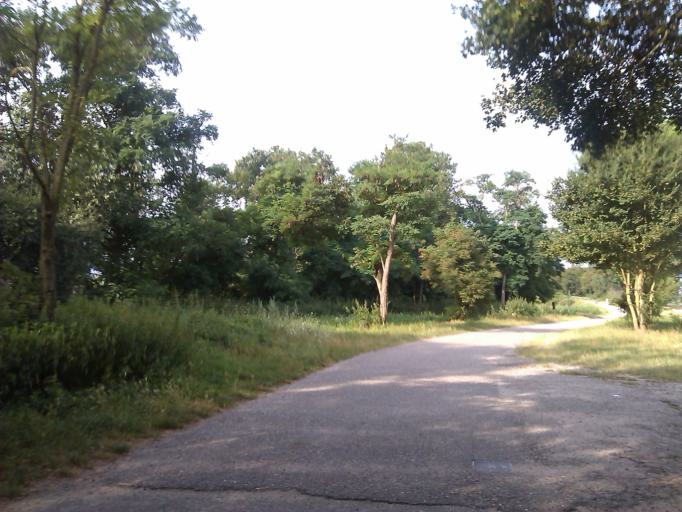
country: DE
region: Rheinland-Pfalz
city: Neuhofen
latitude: 49.4138
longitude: 8.4150
